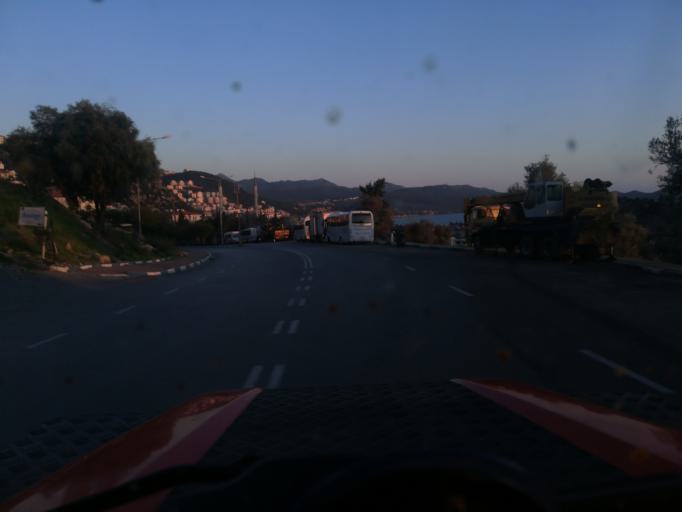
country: TR
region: Antalya
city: Kas
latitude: 36.2048
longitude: 29.6357
